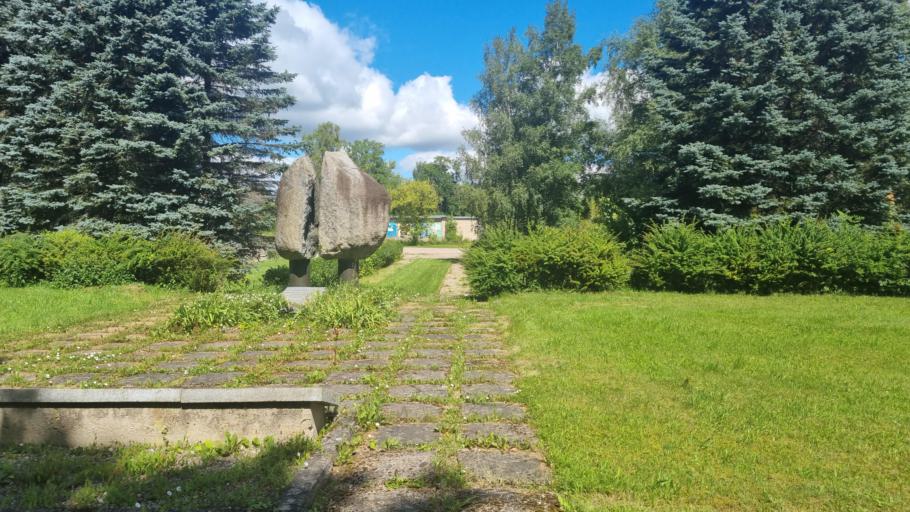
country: LV
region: Daugavpils
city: Daugavpils
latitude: 55.7251
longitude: 26.5511
